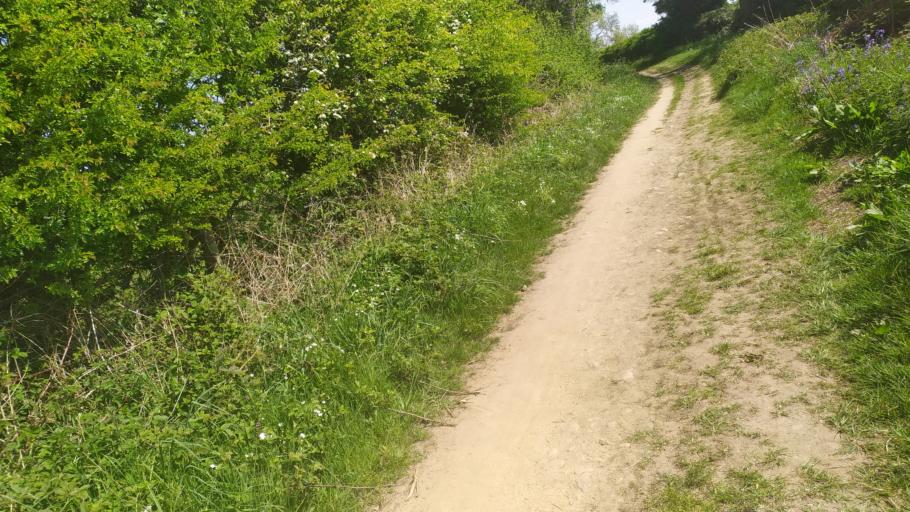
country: GB
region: England
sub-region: City and Borough of Leeds
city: Chapel Allerton
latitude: 53.8803
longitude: -1.5568
